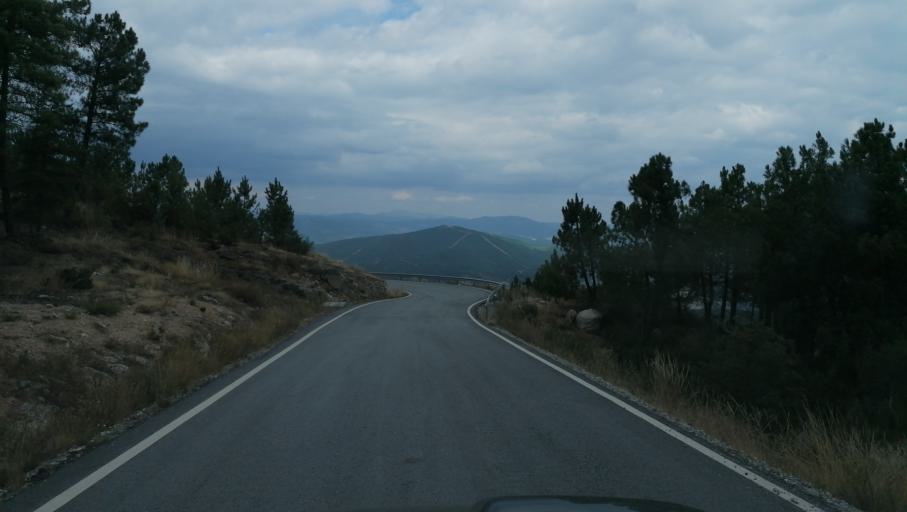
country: PT
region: Vila Real
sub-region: Vila Pouca de Aguiar
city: Vila Pouca de Aguiar
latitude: 41.5467
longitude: -7.6499
